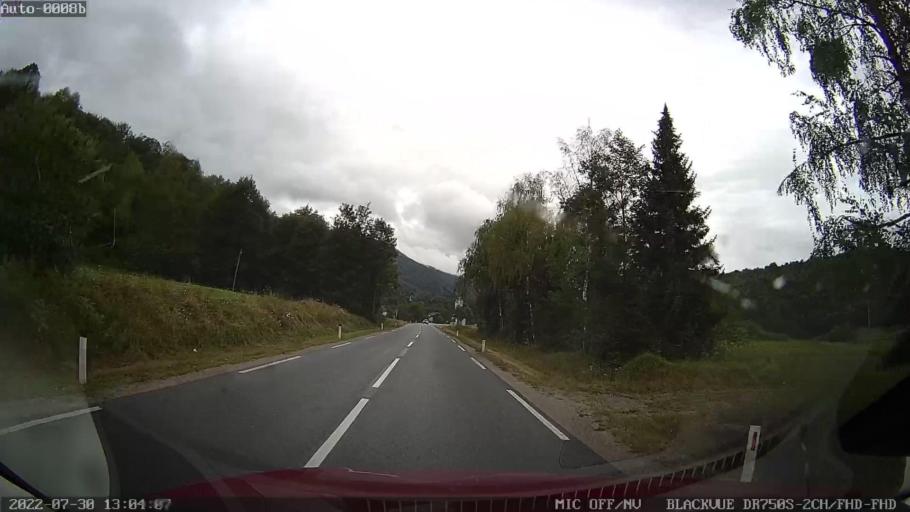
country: SI
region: Semic
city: Semic
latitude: 45.6468
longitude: 15.1458
